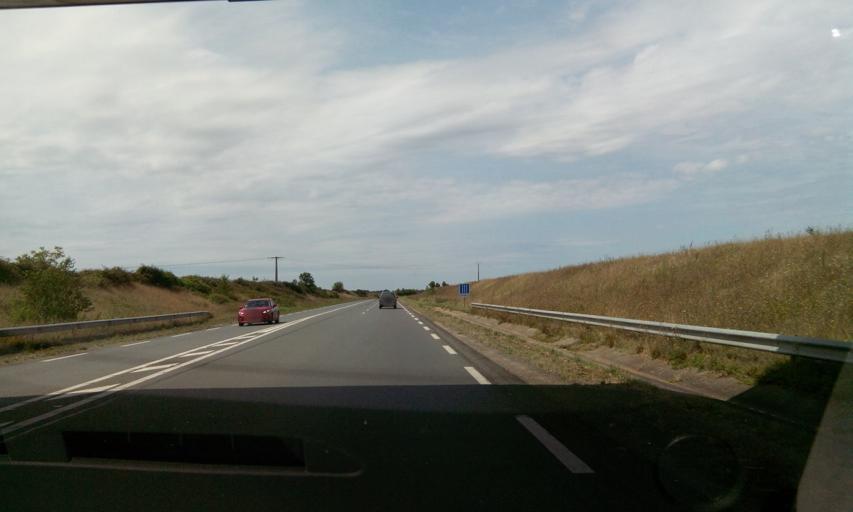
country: FR
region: Poitou-Charentes
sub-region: Departement des Deux-Sevres
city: Vouille
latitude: 46.3002
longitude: -0.3395
